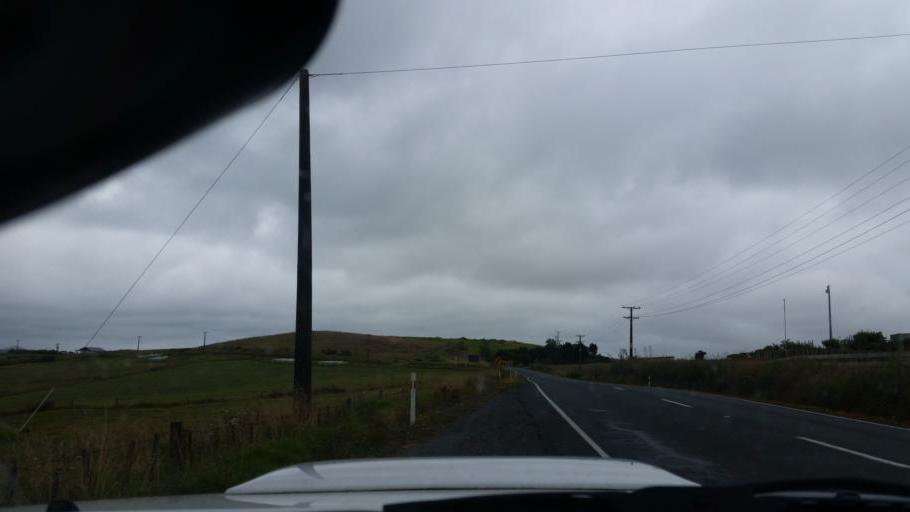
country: NZ
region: Auckland
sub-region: Auckland
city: Wellsford
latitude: -36.1442
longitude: 174.4926
